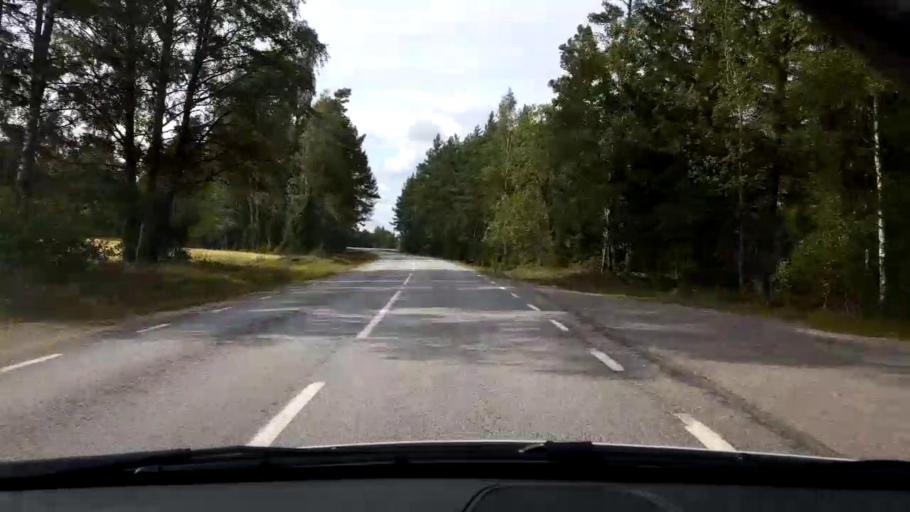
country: SE
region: Joenkoeping
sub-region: Vetlanda Kommun
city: Vetlanda
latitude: 57.3617
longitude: 15.0677
